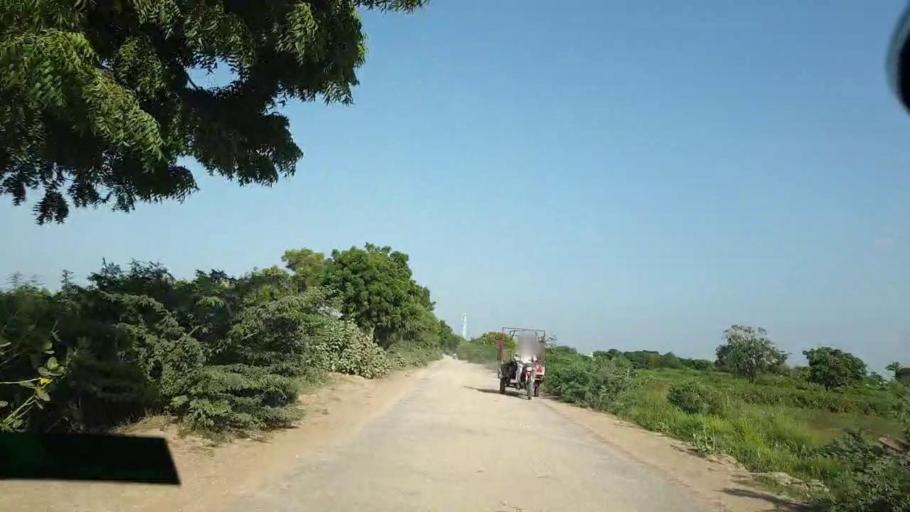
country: PK
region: Sindh
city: Naukot
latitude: 24.7408
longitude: 69.2218
